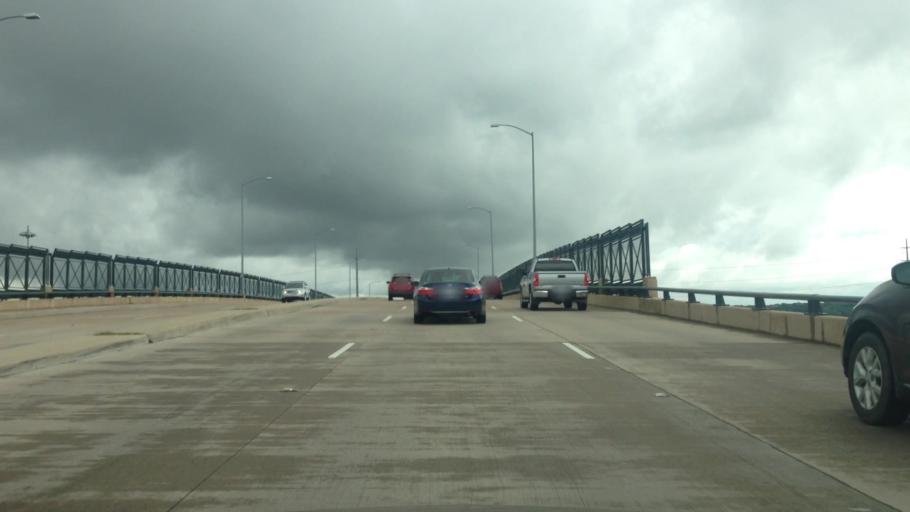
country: US
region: Texas
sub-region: Tarrant County
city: Westworth
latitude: 32.7203
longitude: -97.3866
